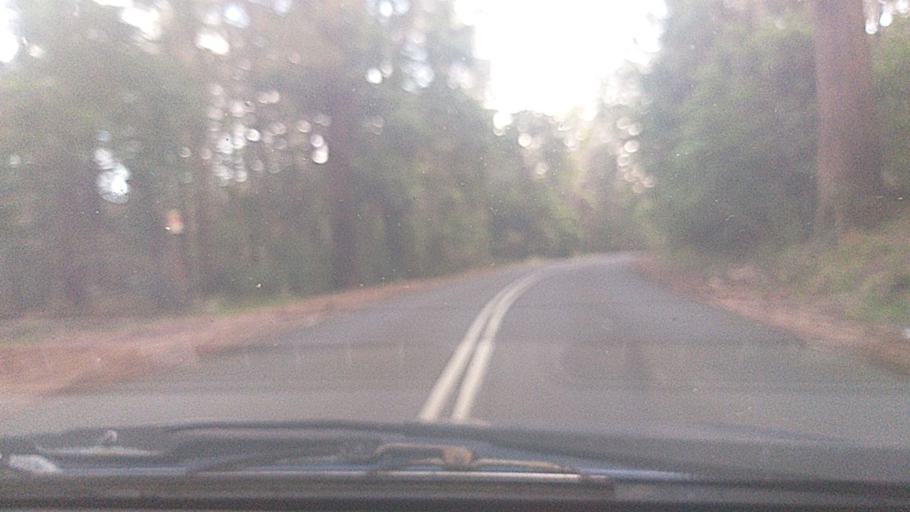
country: AU
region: New South Wales
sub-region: Wollongong
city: Mount Ousley
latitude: -34.3791
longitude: 150.8574
